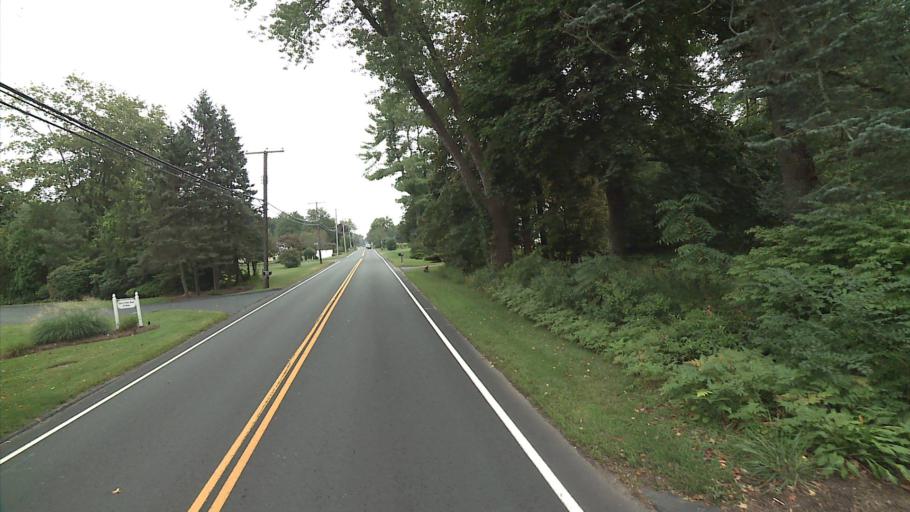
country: US
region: Connecticut
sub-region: Hartford County
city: Windsor
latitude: 41.8659
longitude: -72.6563
